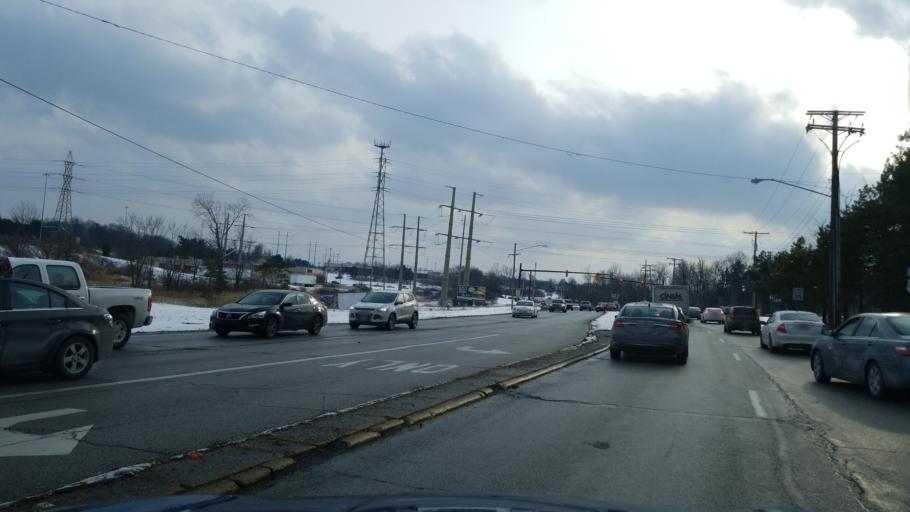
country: US
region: Ohio
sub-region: Cuyahoga County
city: Middleburg Heights
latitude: 41.3543
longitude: -81.8200
